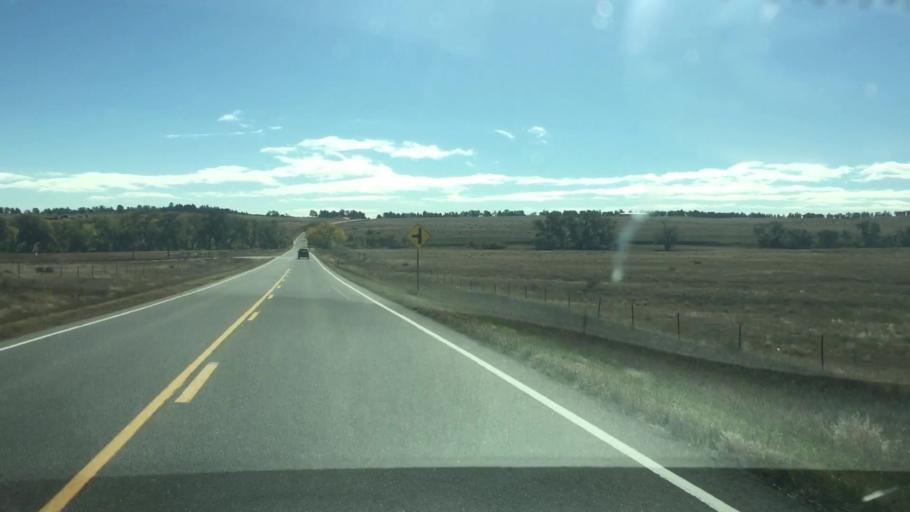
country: US
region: Colorado
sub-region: Elbert County
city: Kiowa
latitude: 39.3221
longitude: -104.3859
